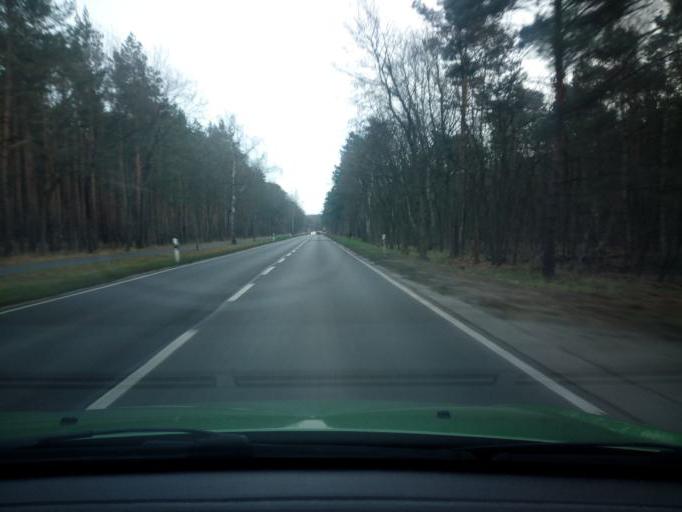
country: DE
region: Berlin
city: Friedrichshagen
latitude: 52.4330
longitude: 13.6075
